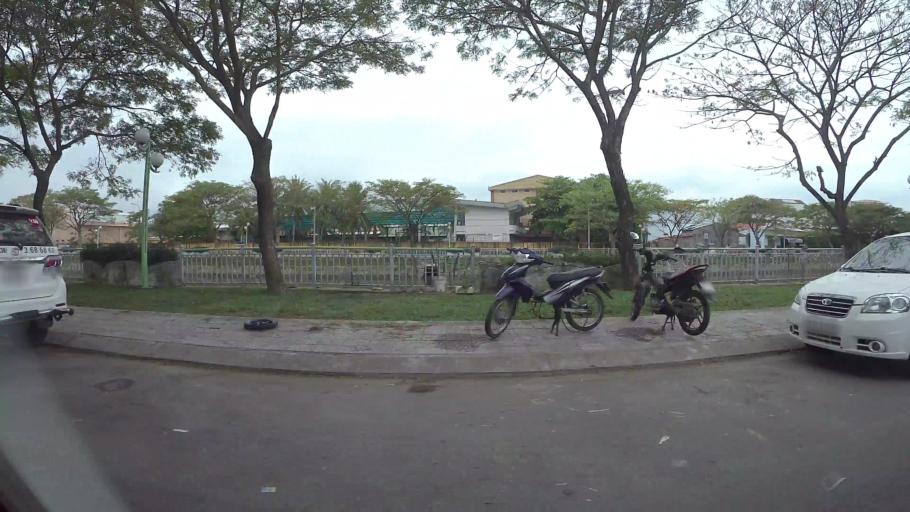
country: VN
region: Da Nang
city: Thanh Khe
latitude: 16.0726
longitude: 108.1811
